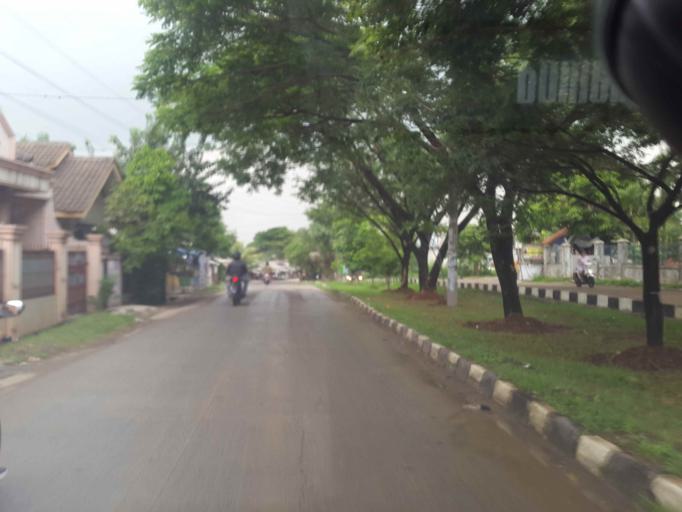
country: ID
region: West Java
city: Cikarang
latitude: -6.3388
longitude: 107.1798
